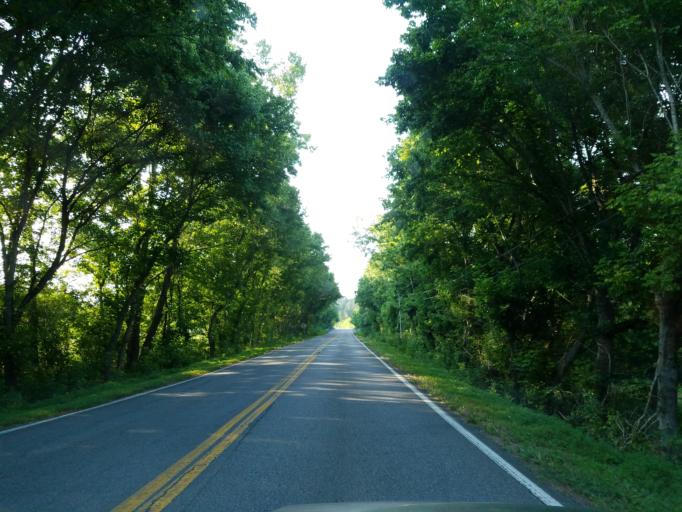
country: US
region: Georgia
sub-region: Pickens County
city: Jasper
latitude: 34.5201
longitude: -84.5235
